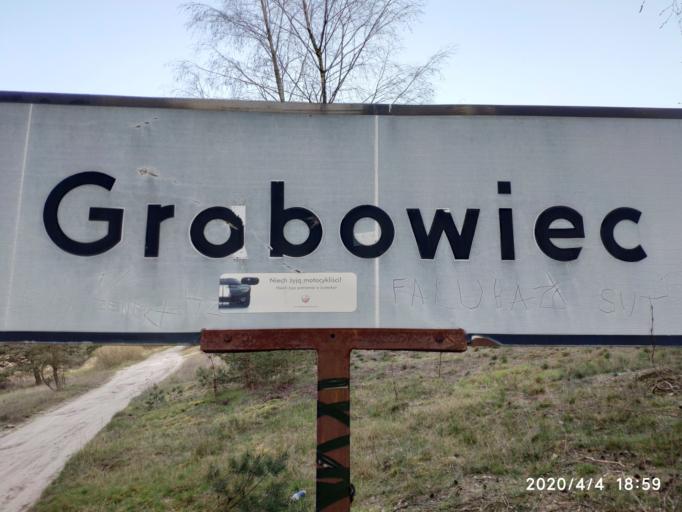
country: PL
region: Lubusz
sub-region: Powiat zielonogorski
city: Nowogrod Bobrzanski
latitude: 51.8950
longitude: 15.2693
